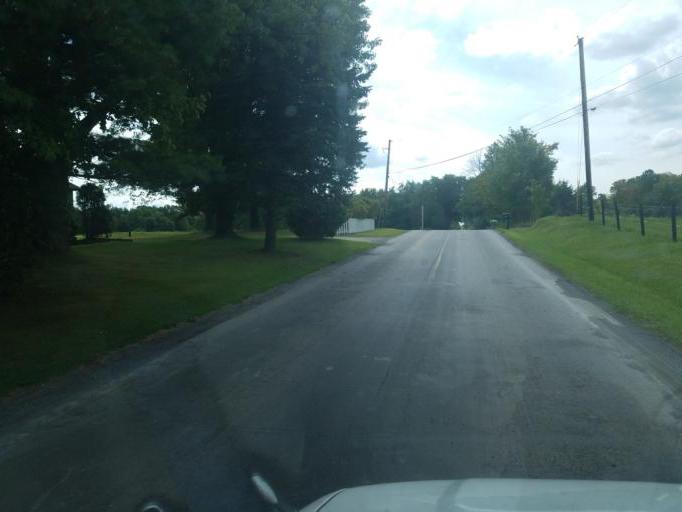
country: US
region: Ohio
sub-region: Geauga County
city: Middlefield
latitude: 41.4553
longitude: -80.9751
